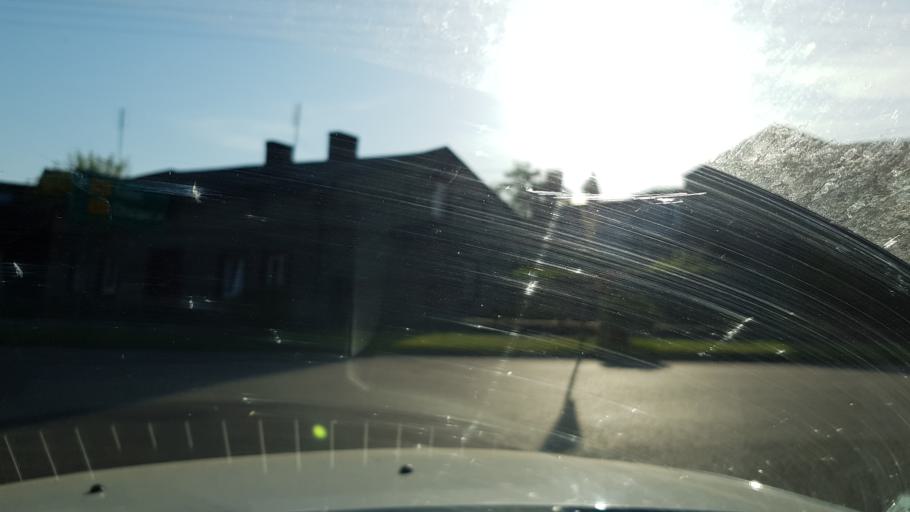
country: PL
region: West Pomeranian Voivodeship
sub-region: Powiat lobeski
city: Dobra
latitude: 53.5825
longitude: 15.3070
